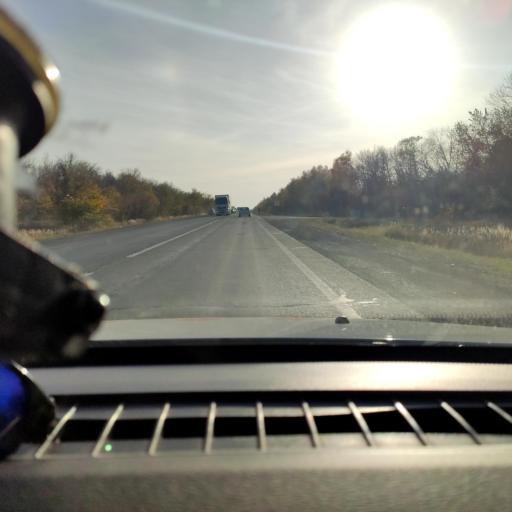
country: RU
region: Samara
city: Chapayevsk
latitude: 52.9902
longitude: 49.8460
